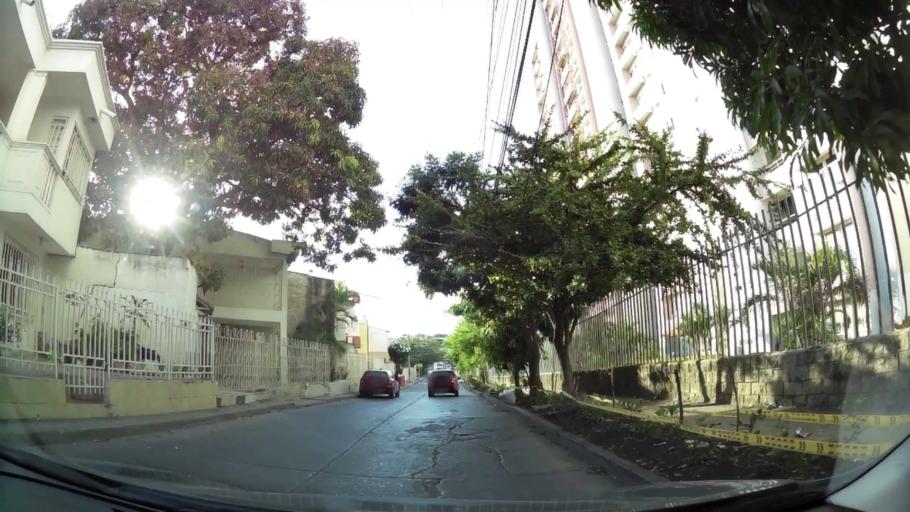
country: CO
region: Bolivar
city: Cartagena
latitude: 10.3879
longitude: -75.4802
